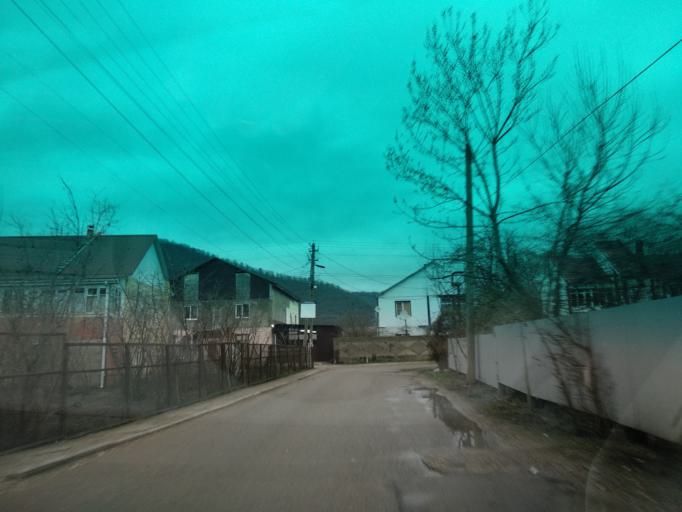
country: RU
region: Krasnodarskiy
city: Novomikhaylovskiy
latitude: 44.2608
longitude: 38.8615
